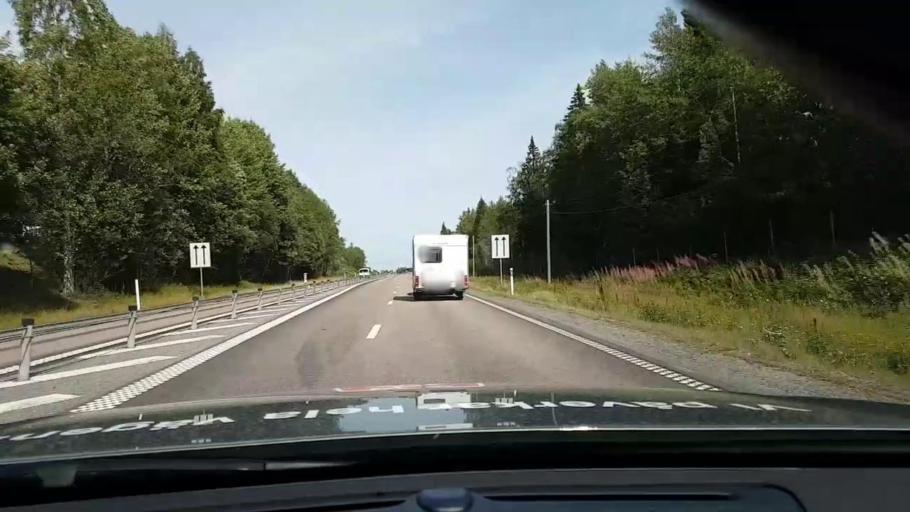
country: SE
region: Vaesternorrland
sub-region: OErnskoeldsviks Kommun
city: Husum
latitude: 63.3627
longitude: 19.1787
